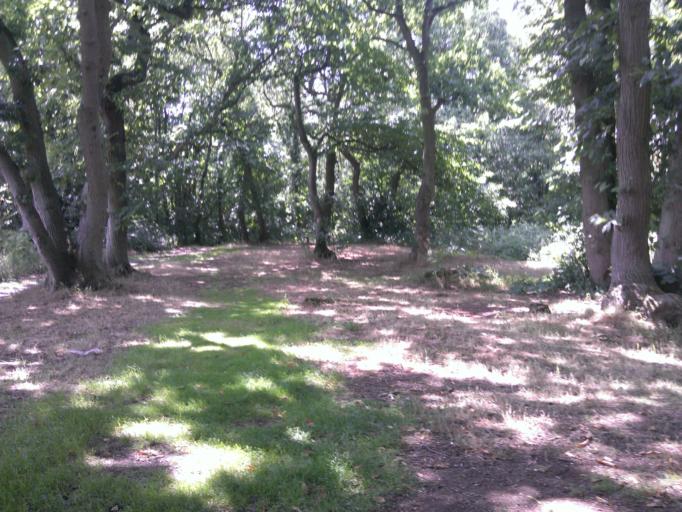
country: GB
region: England
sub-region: Essex
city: Wivenhoe
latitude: 51.8619
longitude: 0.9537
